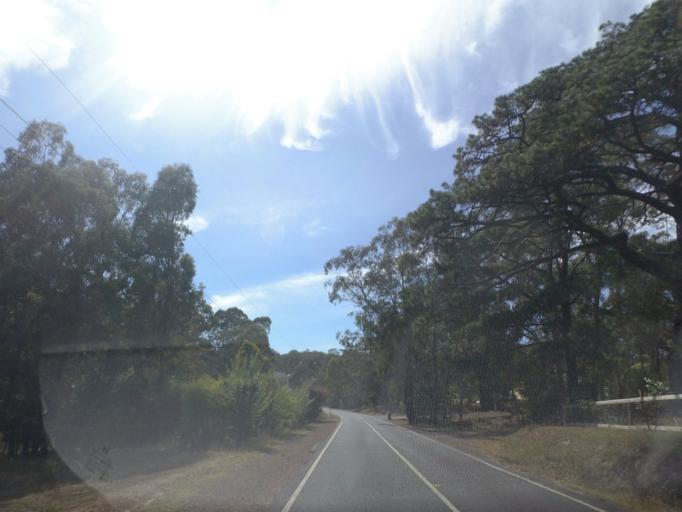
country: AU
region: Victoria
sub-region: Nillumbik
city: Saint Andrews
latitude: -37.6045
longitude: 145.2638
